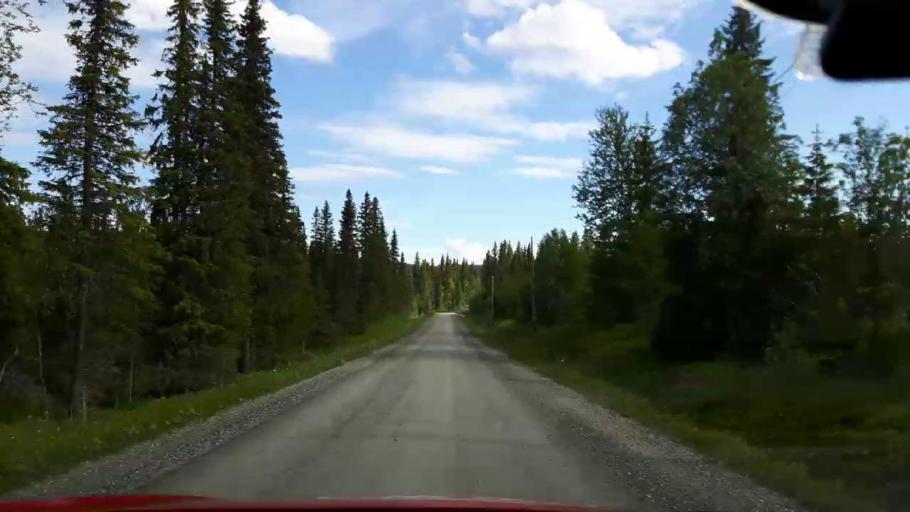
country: SE
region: Jaemtland
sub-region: Krokoms Kommun
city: Valla
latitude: 63.8157
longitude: 14.0470
